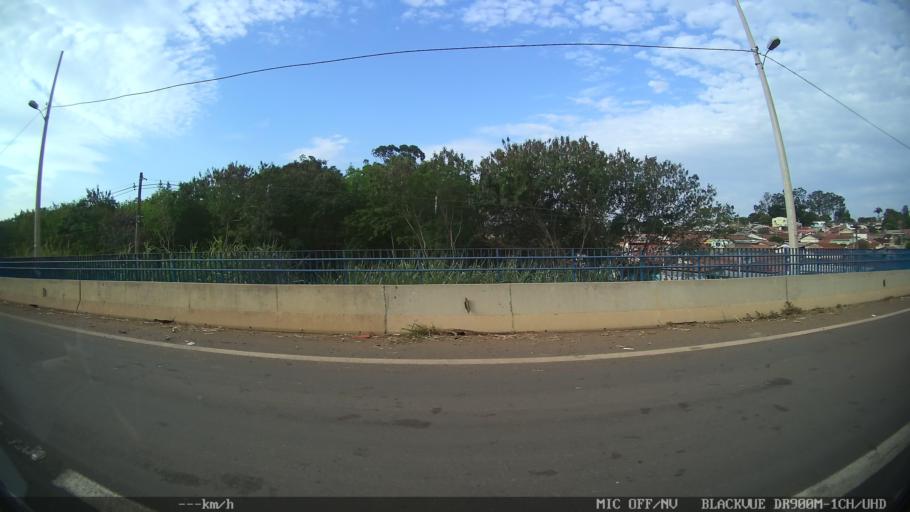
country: BR
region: Sao Paulo
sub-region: Cosmopolis
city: Cosmopolis
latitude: -22.6470
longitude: -47.2068
